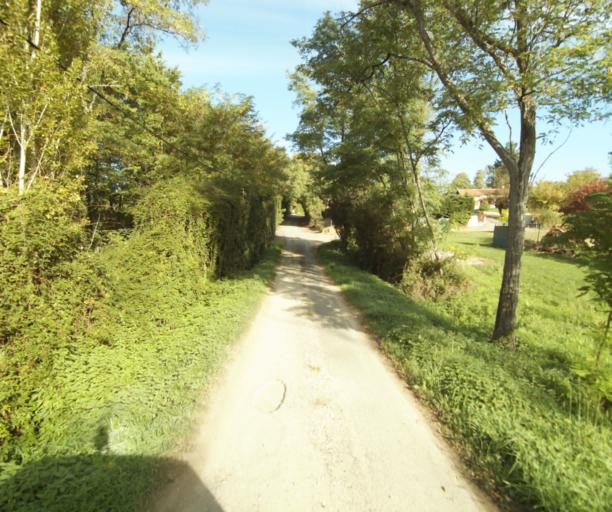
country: FR
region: Midi-Pyrenees
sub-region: Departement du Gers
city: Eauze
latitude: 43.8844
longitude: 0.1408
